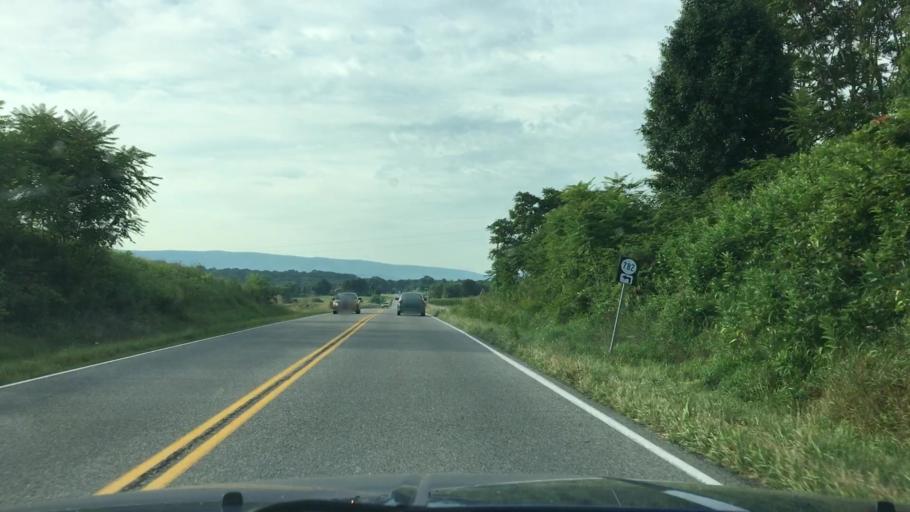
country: US
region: Virginia
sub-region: Augusta County
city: Dooms
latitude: 38.1181
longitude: -78.9101
